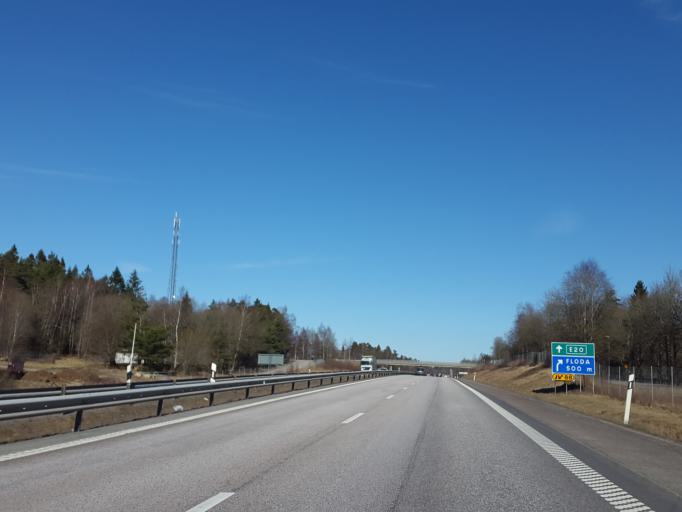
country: SE
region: Vaestra Goetaland
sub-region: Lerums Kommun
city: Stenkullen
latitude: 57.7953
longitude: 12.3526
